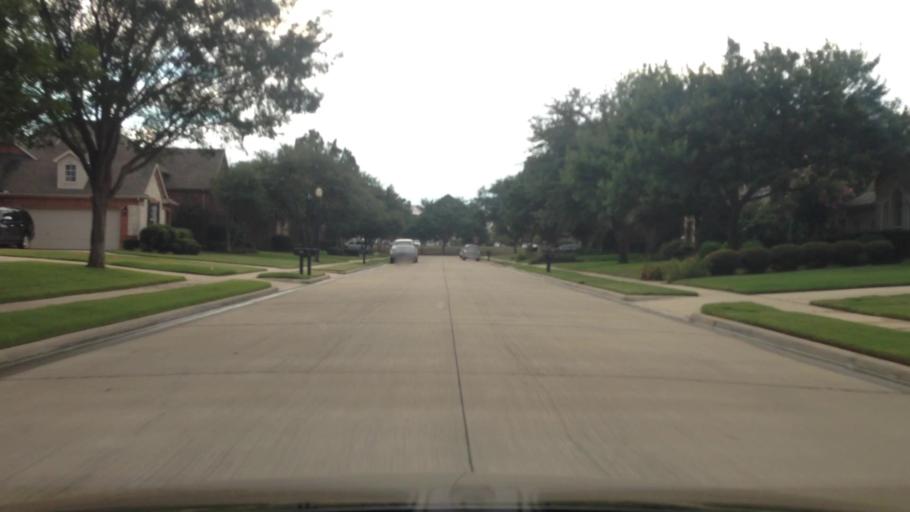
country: US
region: Texas
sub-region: Denton County
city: Flower Mound
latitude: 33.0044
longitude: -97.0442
